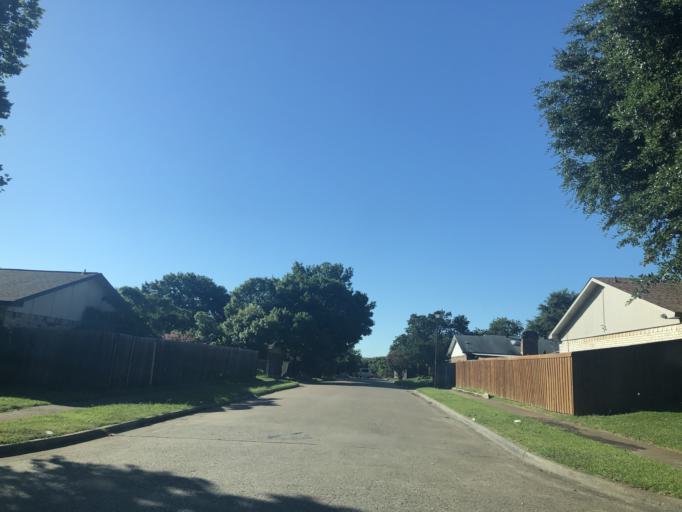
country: US
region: Texas
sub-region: Dallas County
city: Duncanville
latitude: 32.6385
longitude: -96.9502
